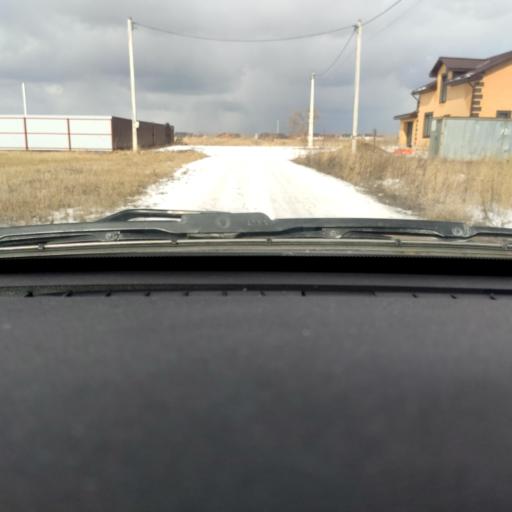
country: RU
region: Voronezj
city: Novaya Usman'
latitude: 51.6605
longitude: 39.4621
